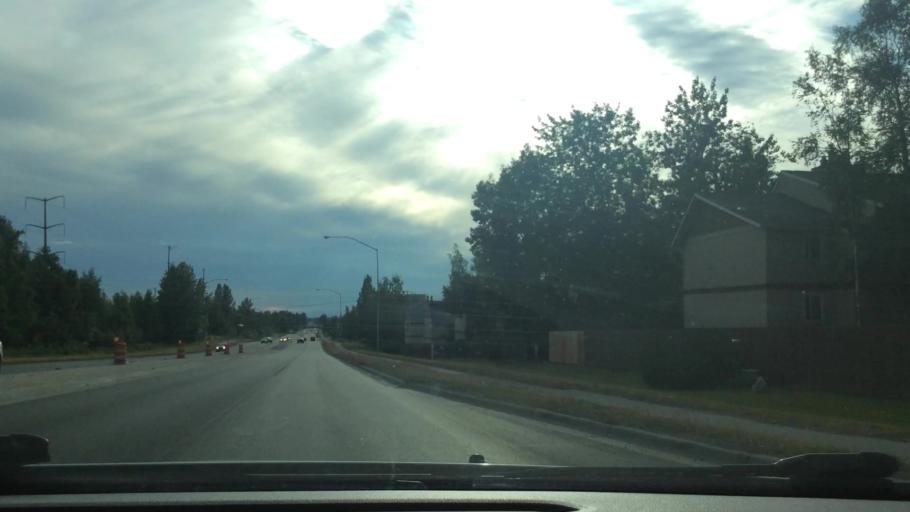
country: US
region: Alaska
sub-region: Anchorage Municipality
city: Anchorage
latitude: 61.1809
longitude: -149.7875
